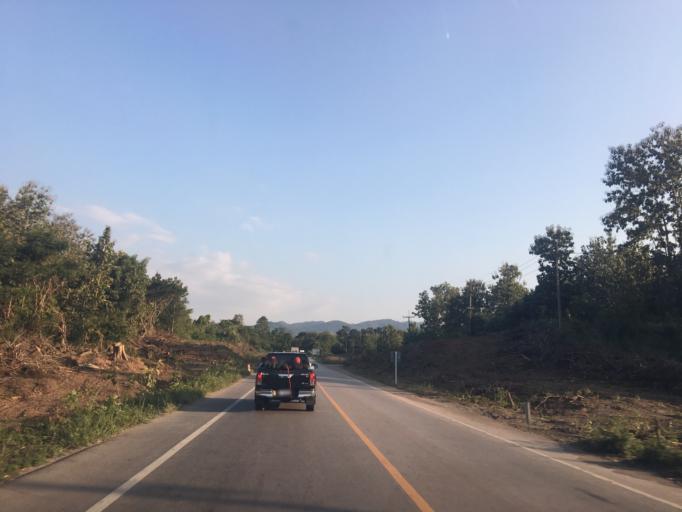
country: TH
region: Lampang
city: Ngao
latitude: 18.6175
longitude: 100.0240
